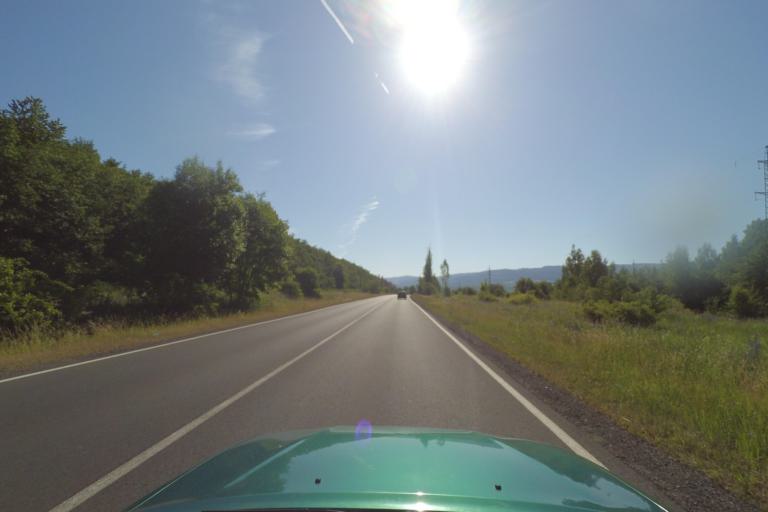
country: CZ
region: Karlovarsky
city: Bukovany
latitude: 50.1576
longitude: 12.5971
